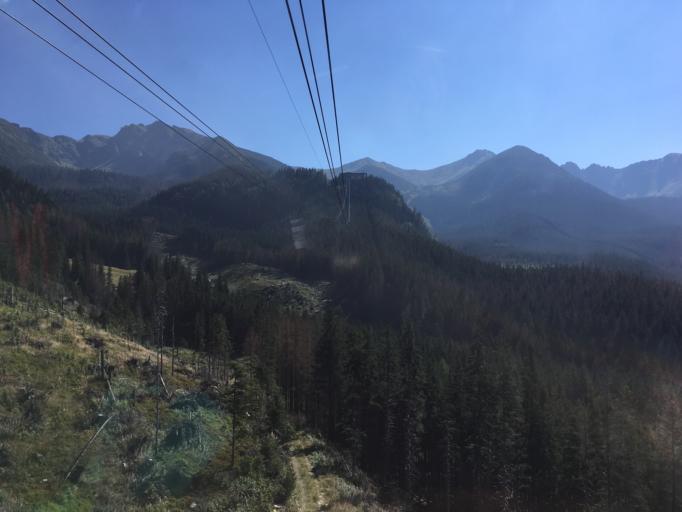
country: PL
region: Lesser Poland Voivodeship
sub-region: Powiat tatrzanski
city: Zakopane
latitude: 49.2604
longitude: 19.9764
